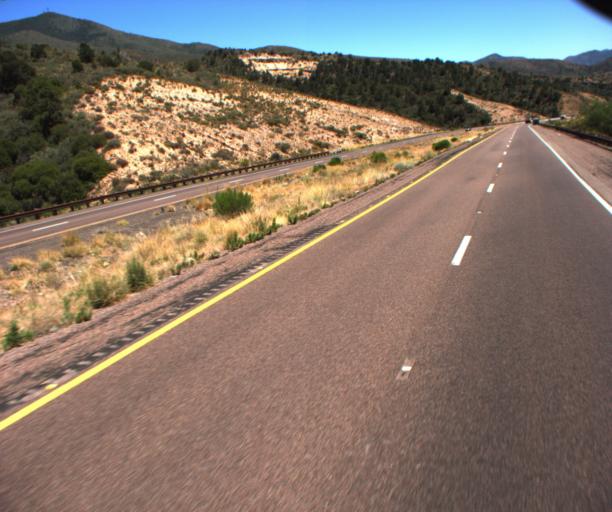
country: US
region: Arizona
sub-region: Gila County
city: Tonto Basin
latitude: 33.9171
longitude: -111.4539
